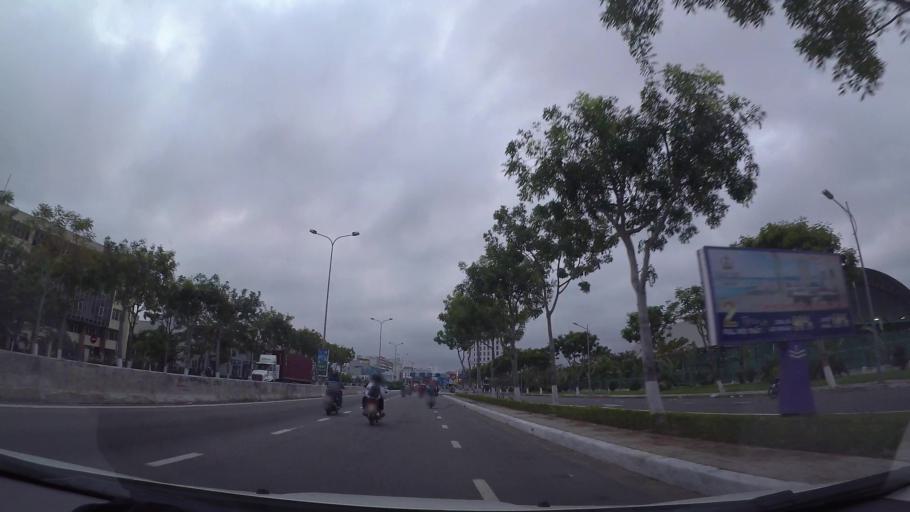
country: VN
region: Da Nang
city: Cam Le
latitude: 16.0335
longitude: 108.2264
